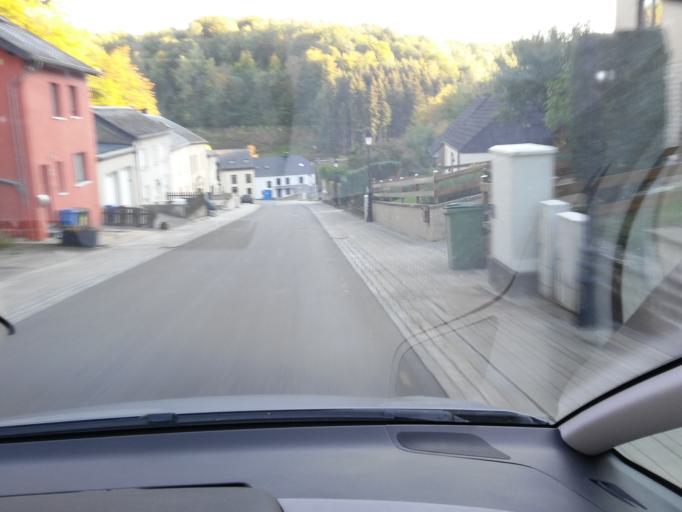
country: LU
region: Luxembourg
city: Eischen
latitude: 49.6832
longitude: 5.8668
